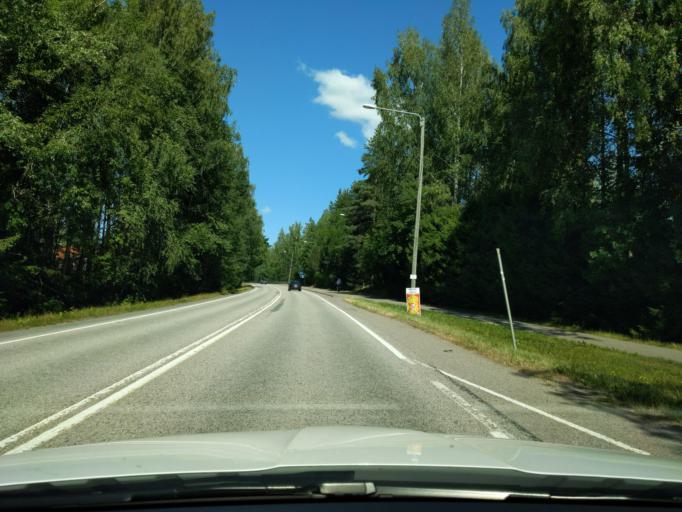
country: FI
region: Uusimaa
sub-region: Helsinki
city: Nurmijaervi
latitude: 60.5224
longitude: 24.7536
